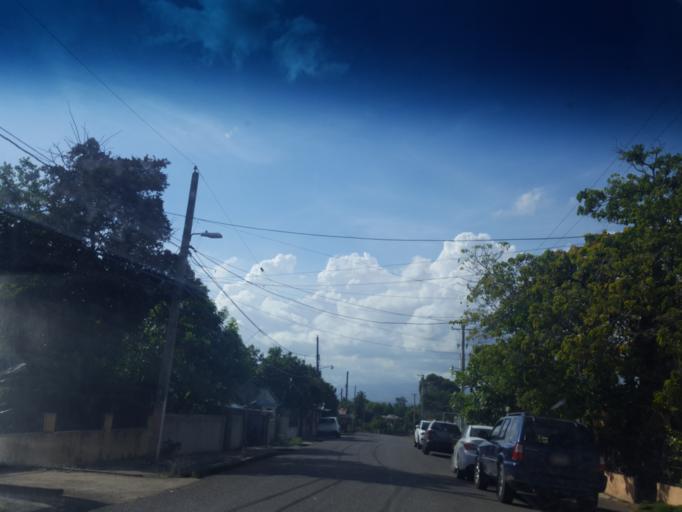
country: DO
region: Santiago
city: Licey al Medio
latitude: 19.3706
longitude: -70.6075
